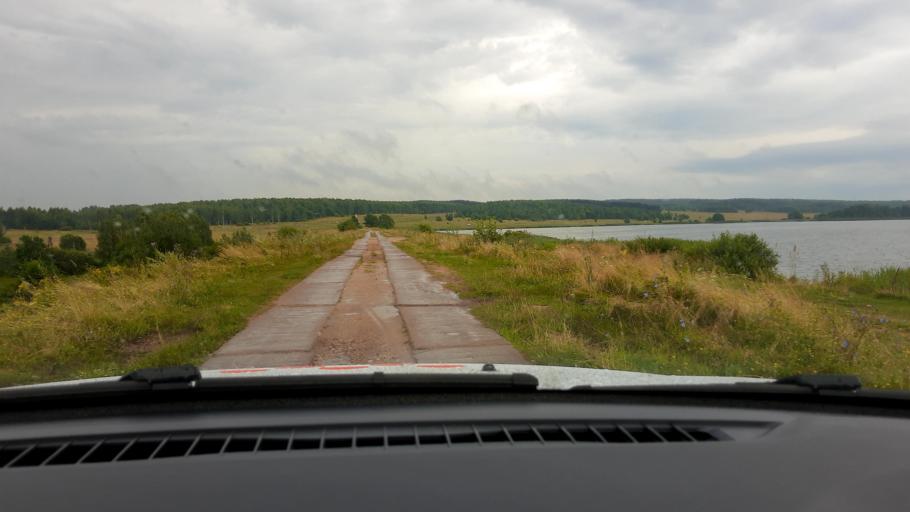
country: RU
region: Nizjnij Novgorod
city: Surovatikha
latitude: 55.9372
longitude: 43.9169
